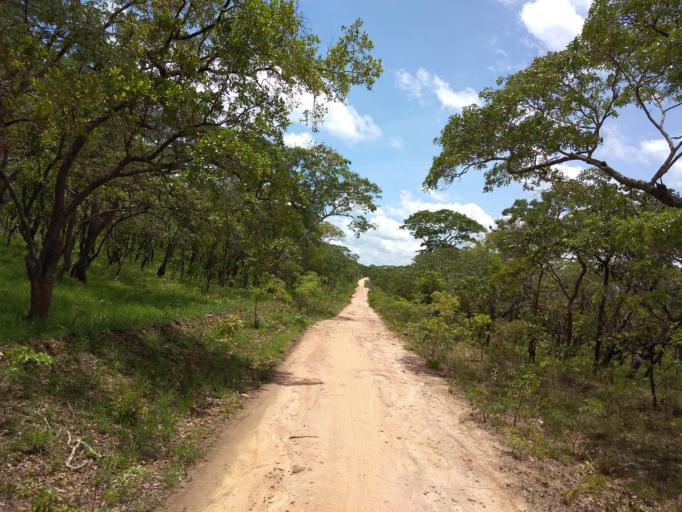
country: ZM
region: Central
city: Mkushi
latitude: -13.9257
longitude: 29.8645
